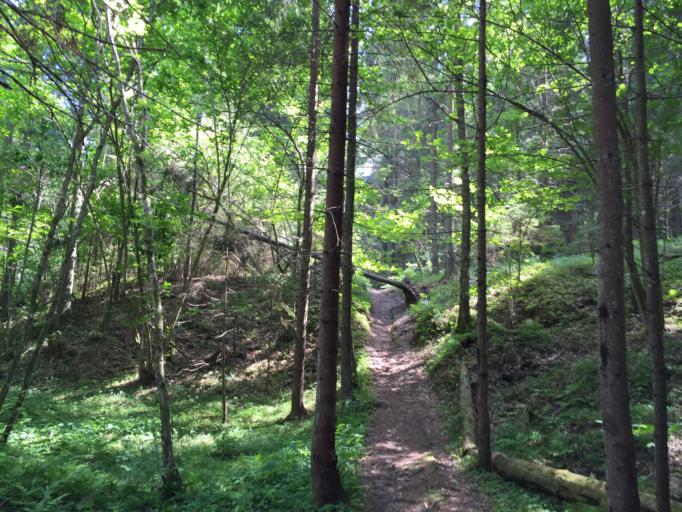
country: LV
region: Ligatne
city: Ligatne
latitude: 57.2537
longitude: 25.0631
